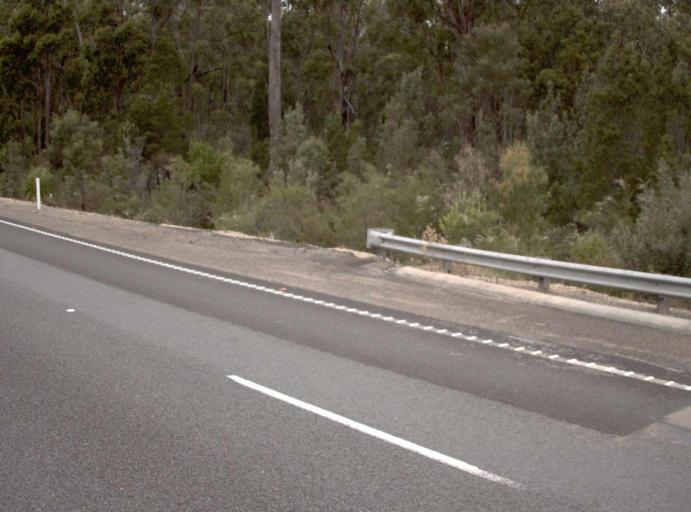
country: AU
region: Victoria
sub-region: East Gippsland
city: Lakes Entrance
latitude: -37.6933
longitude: 147.9991
